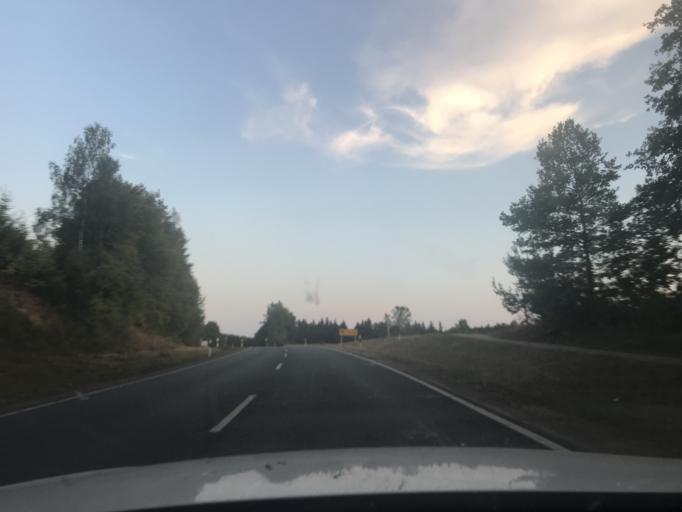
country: DE
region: Bavaria
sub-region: Upper Franconia
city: Creussen
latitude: 49.8760
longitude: 11.6116
